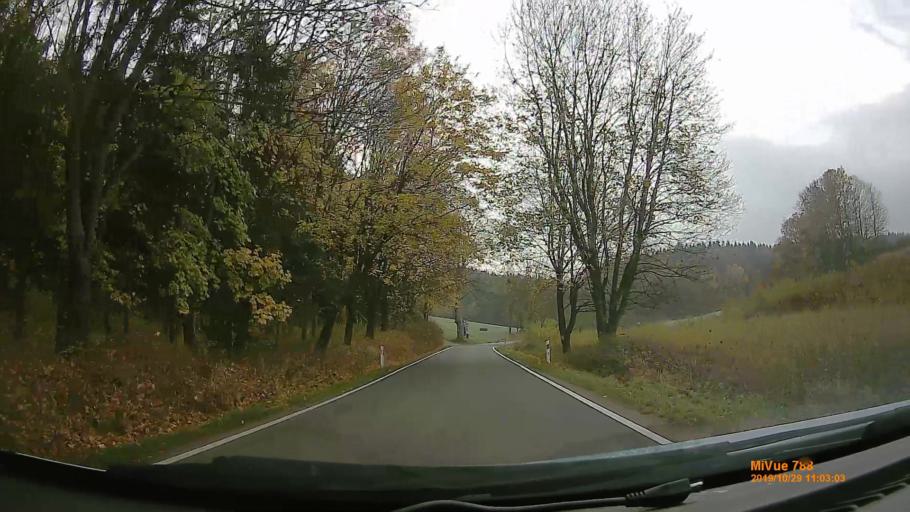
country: PL
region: Lower Silesian Voivodeship
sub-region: Powiat klodzki
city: Radkow
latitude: 50.4869
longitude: 16.4676
